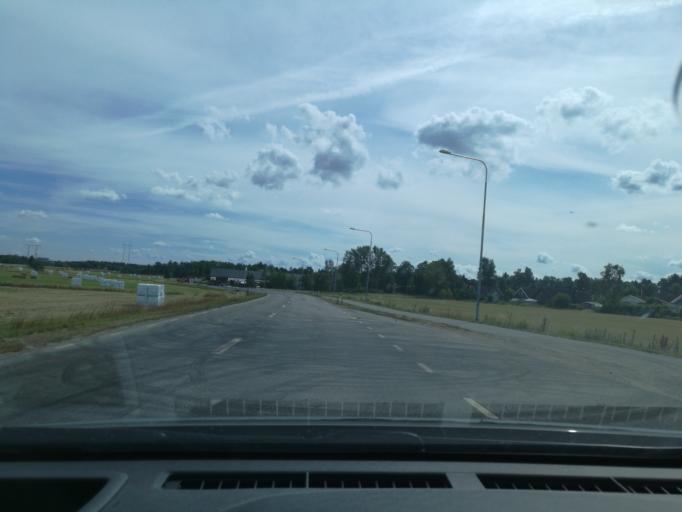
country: SE
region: Stockholm
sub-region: Sigtuna Kommun
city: Rosersberg
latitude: 59.5900
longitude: 17.8913
